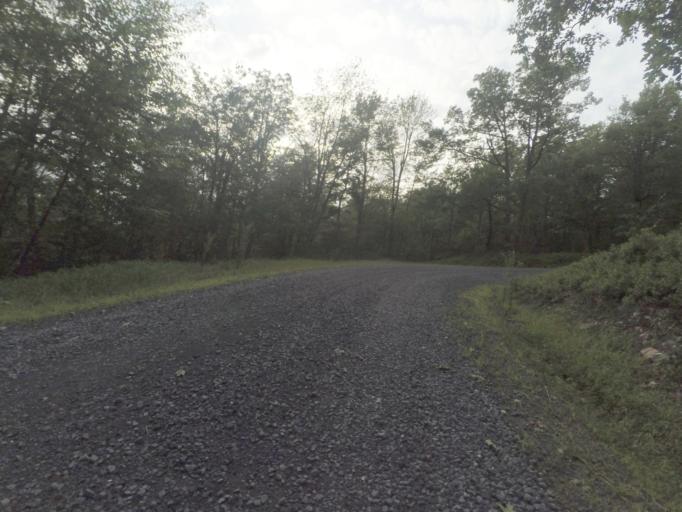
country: US
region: Pennsylvania
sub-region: Centre County
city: Boalsburg
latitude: 40.7185
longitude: -77.7952
